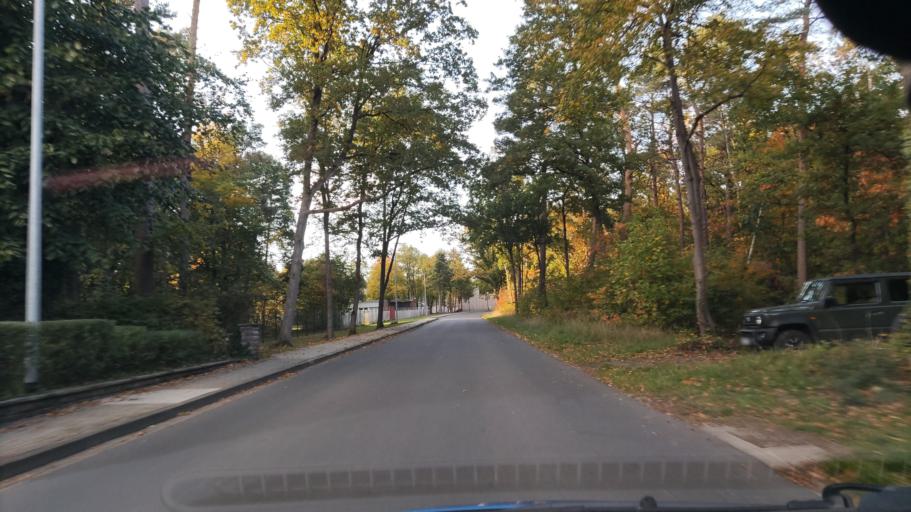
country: DE
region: Lower Saxony
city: Munster
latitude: 52.9794
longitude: 10.0779
